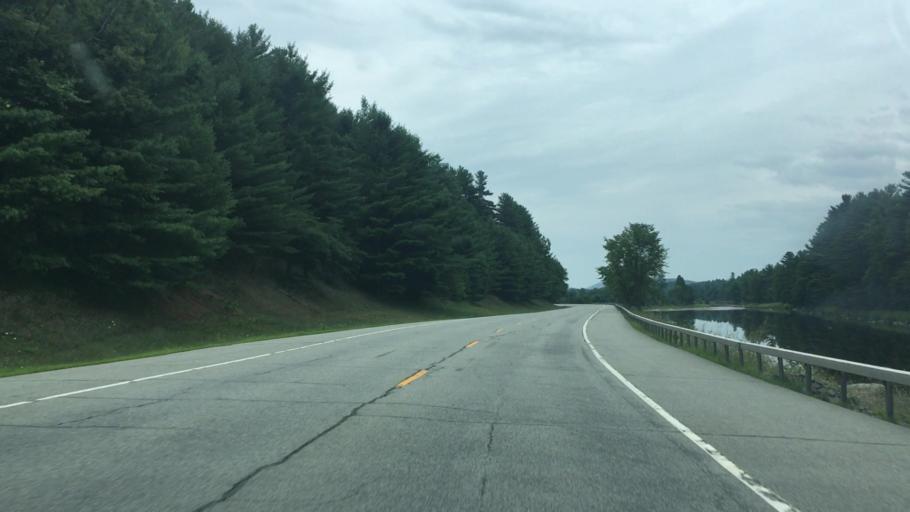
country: US
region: New York
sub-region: Essex County
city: Elizabethtown
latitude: 44.3539
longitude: -73.7535
